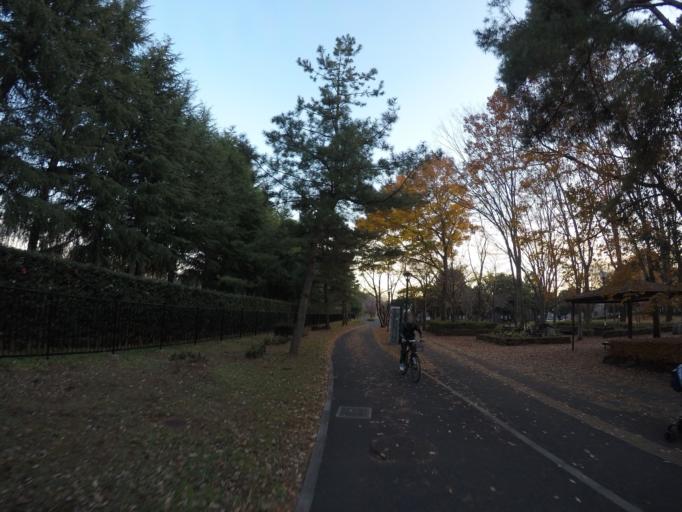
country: JP
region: Ibaraki
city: Naka
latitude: 36.0674
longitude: 140.1228
